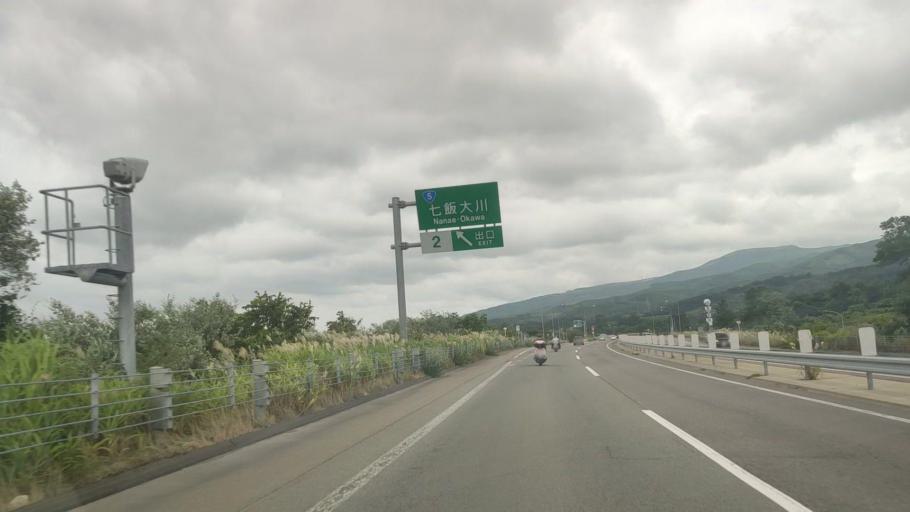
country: JP
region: Hokkaido
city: Nanae
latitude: 41.8644
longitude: 140.7307
